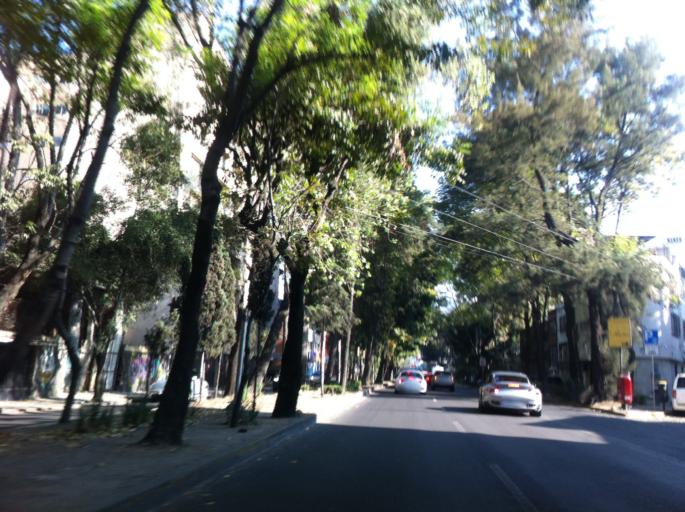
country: MX
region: Mexico City
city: Miguel Hidalgo
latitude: 19.4370
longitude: -99.1828
